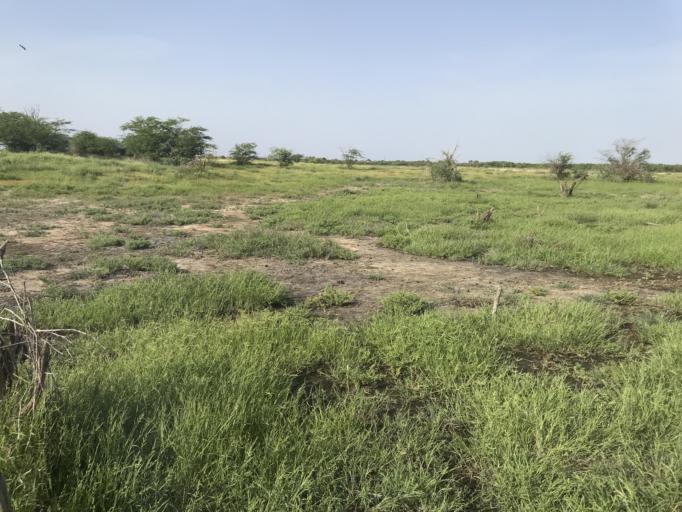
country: SN
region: Saint-Louis
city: Saint-Louis
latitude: 15.9297
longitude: -16.4602
